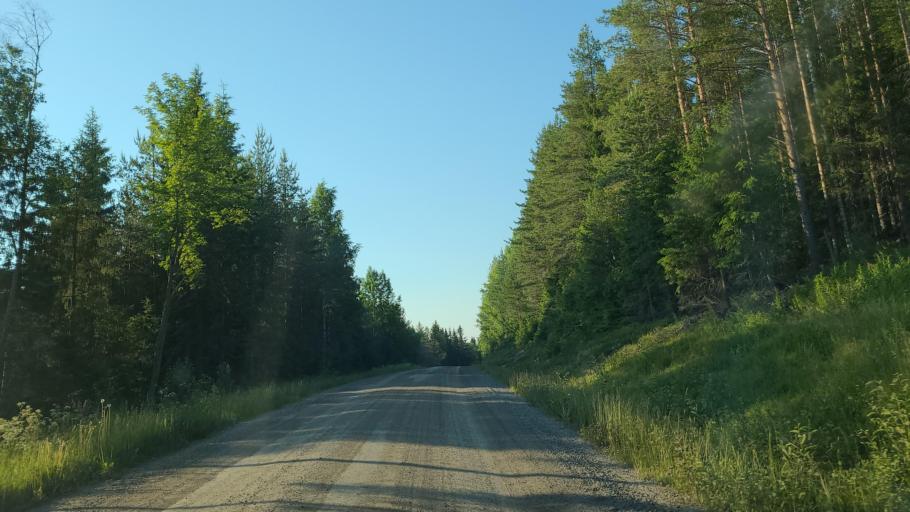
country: SE
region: Vaesterbotten
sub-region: Skelleftea Kommun
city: Burea
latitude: 64.3525
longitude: 21.3529
